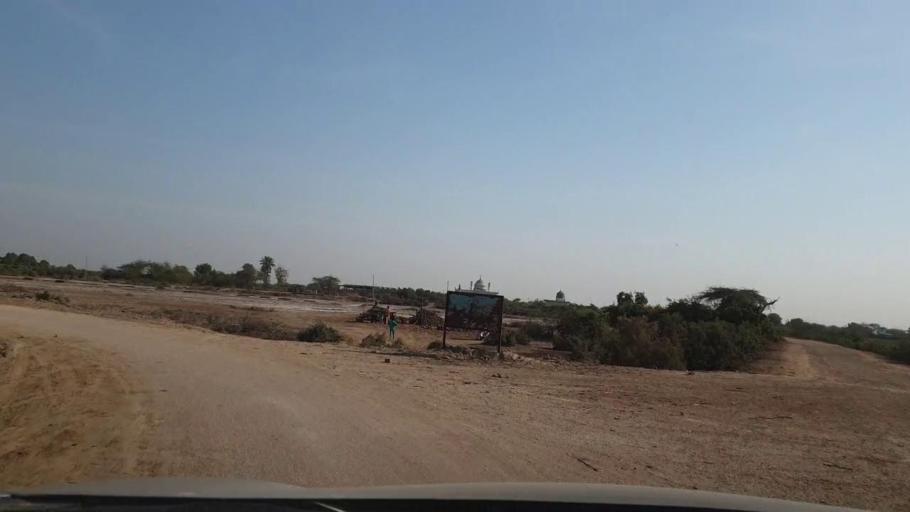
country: PK
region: Sindh
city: Berani
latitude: 25.7344
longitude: 68.7987
